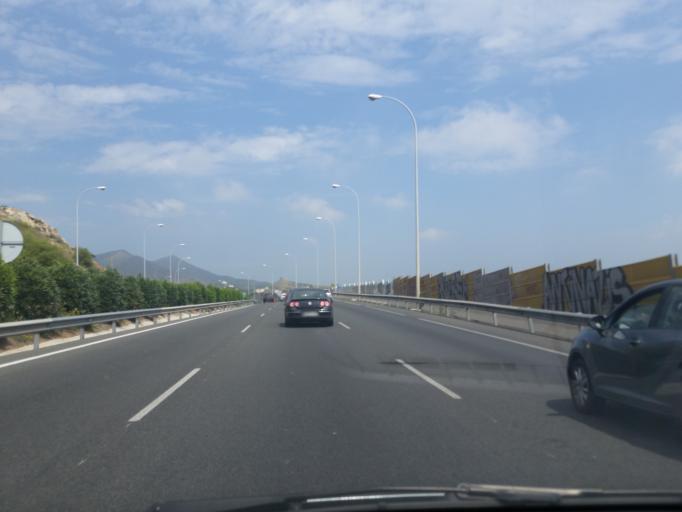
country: ES
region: Andalusia
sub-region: Provincia de Malaga
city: Malaga
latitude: 36.7321
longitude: -4.4540
